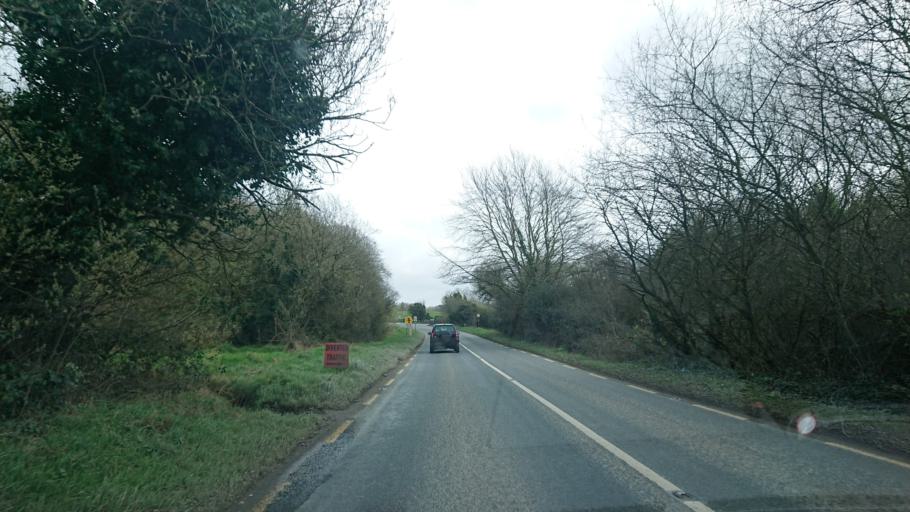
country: IE
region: Leinster
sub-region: Kildare
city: Johnstown
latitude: 53.2010
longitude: -6.6213
